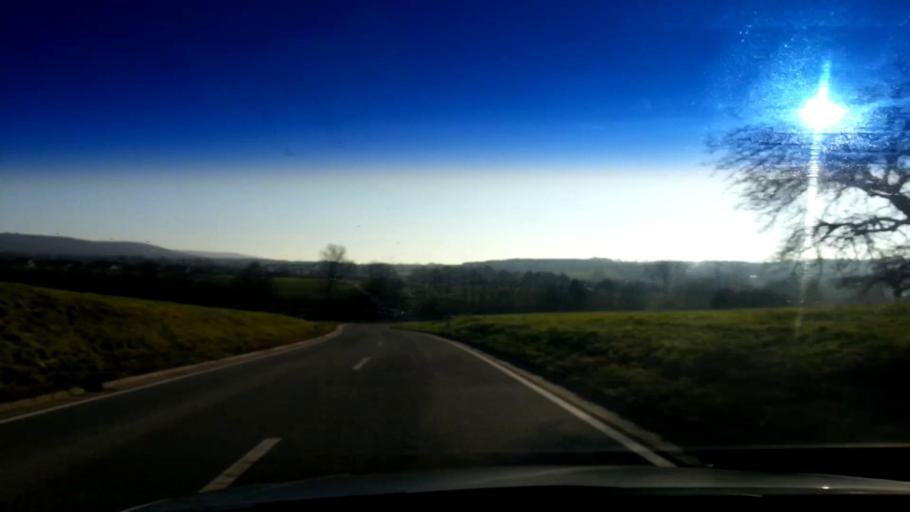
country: DE
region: Bavaria
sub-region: Upper Franconia
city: Litzendorf
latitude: 49.9182
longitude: 10.9974
